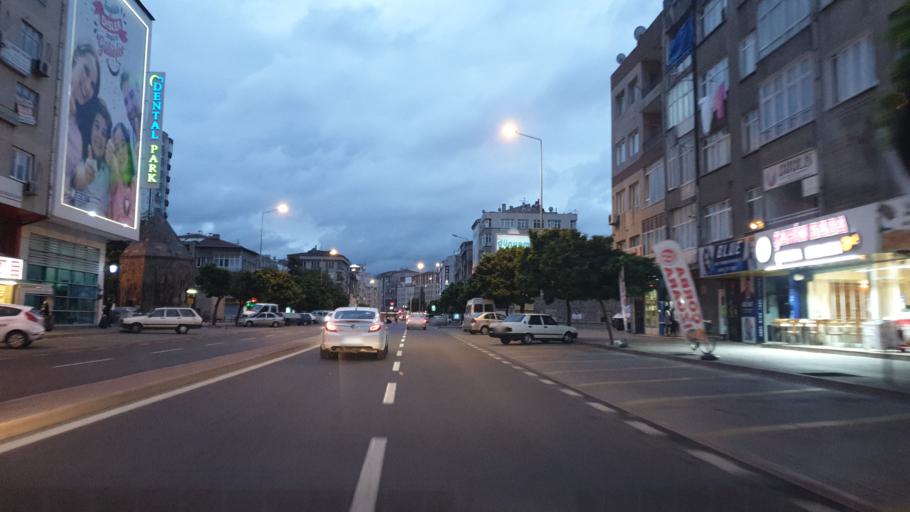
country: TR
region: Kayseri
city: Kayseri
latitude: 38.7234
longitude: 35.4814
